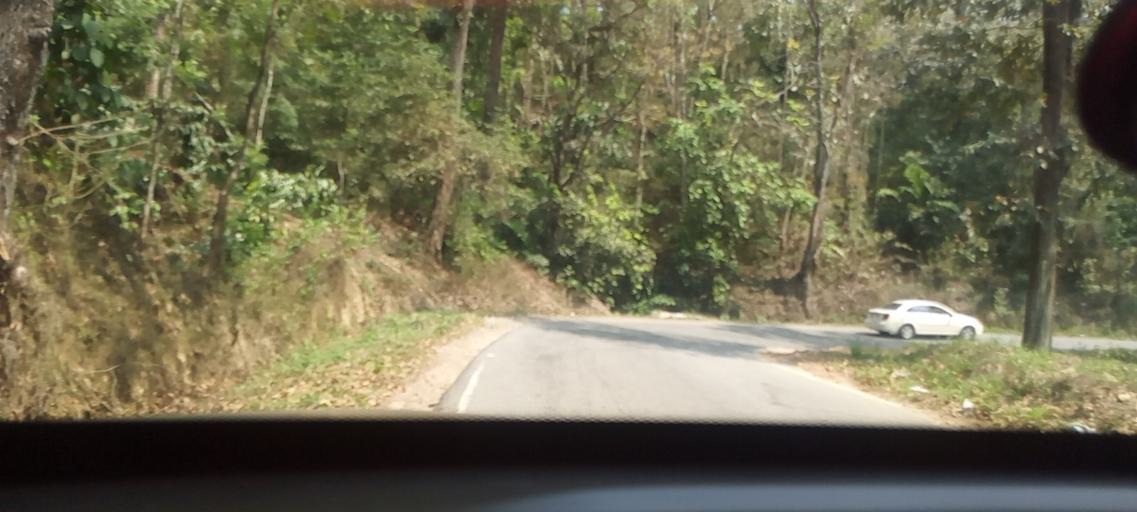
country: IN
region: Karnataka
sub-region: Chikmagalur
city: Mudigere
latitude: 13.2728
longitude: 75.6118
